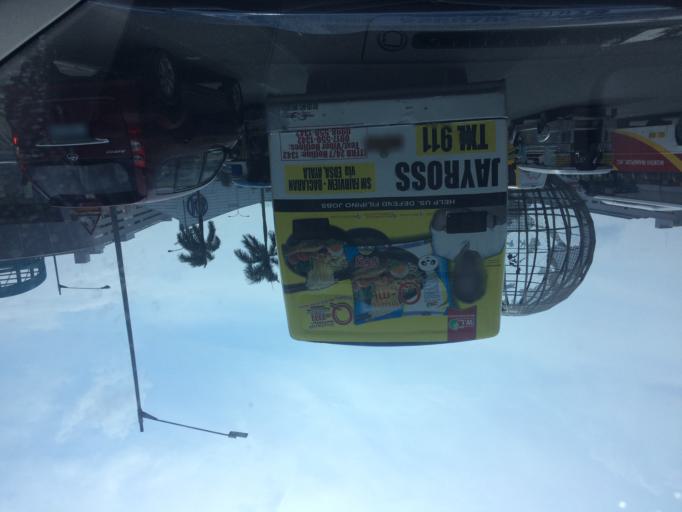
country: PH
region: Metro Manila
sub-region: Makati City
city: Makati City
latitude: 14.5356
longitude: 120.9852
